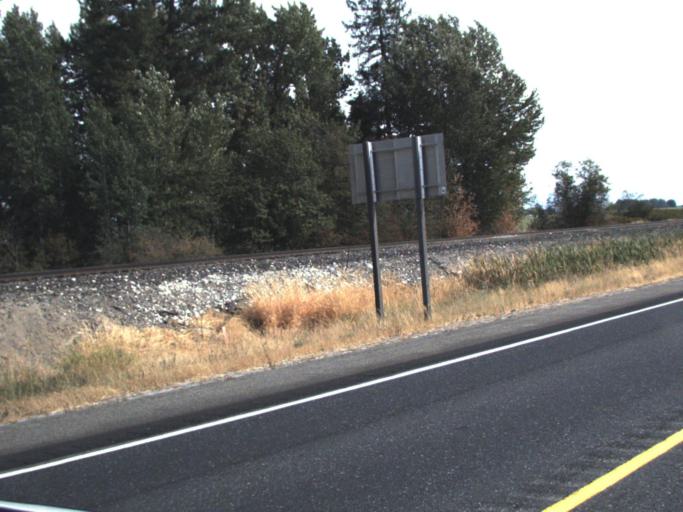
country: US
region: Washington
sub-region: Spokane County
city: Deer Park
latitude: 47.9879
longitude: -117.5375
